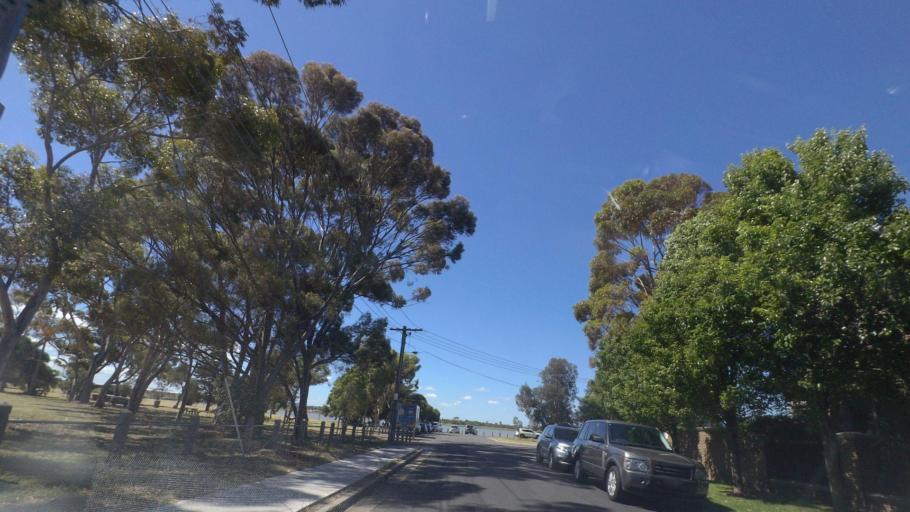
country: AU
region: Victoria
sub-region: Hobsons Bay
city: Altona
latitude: -37.8625
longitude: 144.8335
